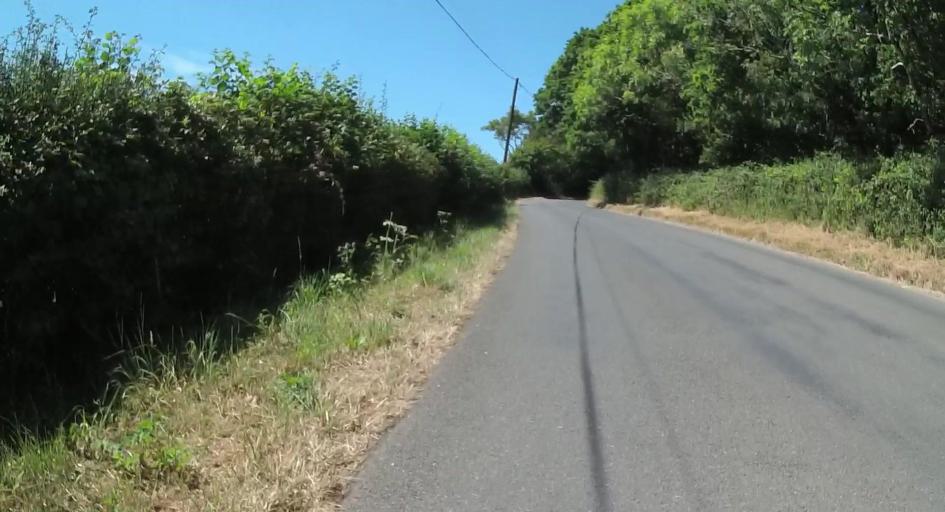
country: GB
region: England
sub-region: Dorset
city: Wareham
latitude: 50.6321
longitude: -2.1035
